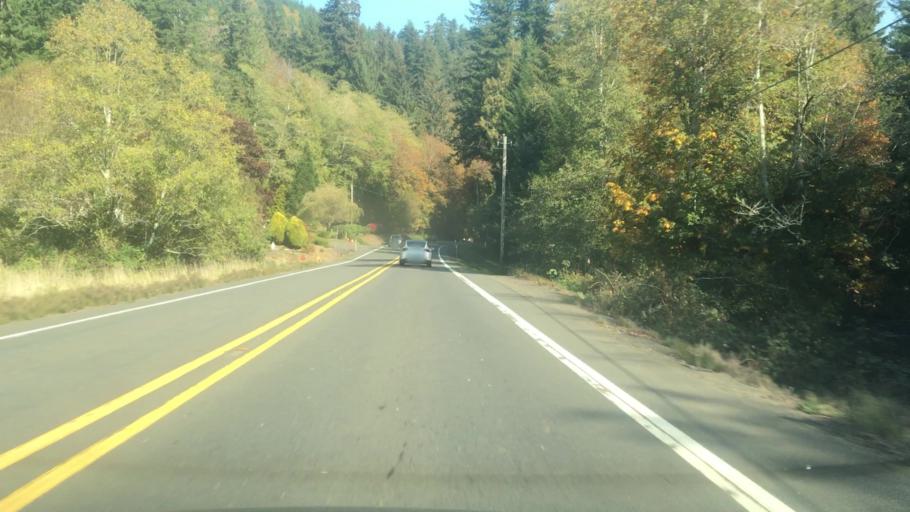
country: US
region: Oregon
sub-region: Lincoln County
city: Rose Lodge
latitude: 45.0246
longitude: -123.8267
